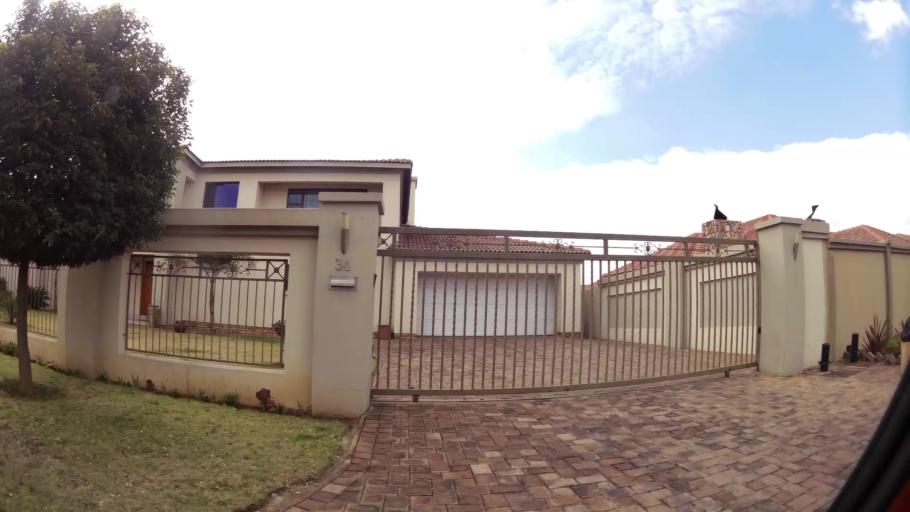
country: ZA
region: Gauteng
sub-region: Sedibeng District Municipality
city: Vanderbijlpark
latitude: -26.7275
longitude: 27.8700
